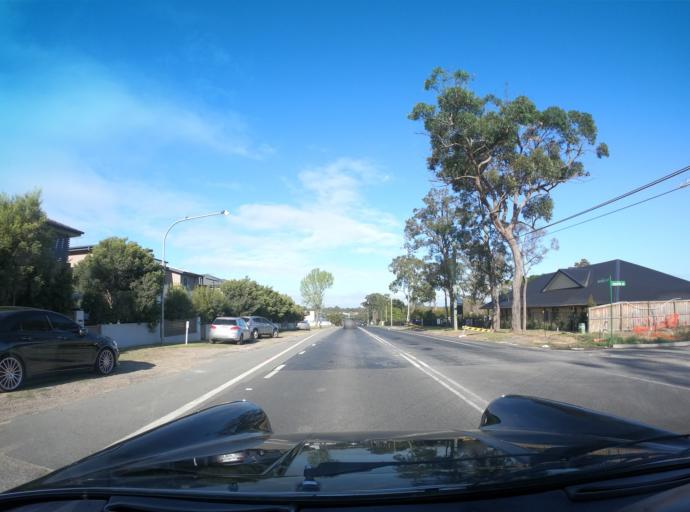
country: AU
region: New South Wales
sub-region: The Hills Shire
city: Beaumont Hills
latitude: -33.6866
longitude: 150.9482
